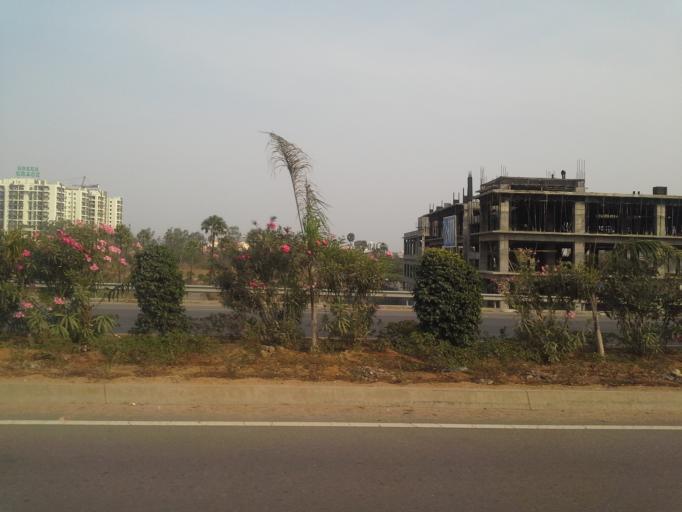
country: IN
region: Telangana
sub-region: Rangareddi
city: Kukatpalli
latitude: 17.4198
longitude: 78.3564
